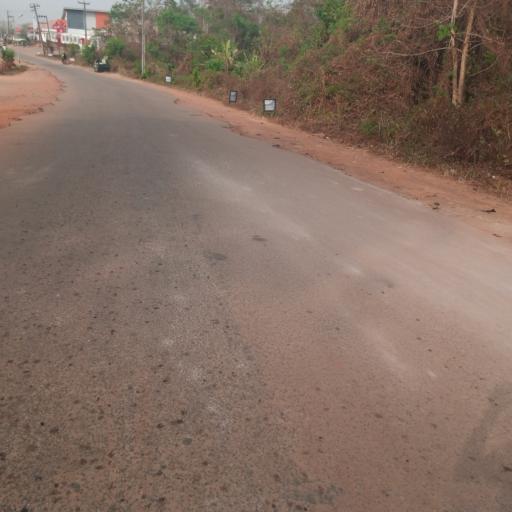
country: NG
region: Ondo
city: Ilare
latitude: 7.2994
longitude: 5.1391
